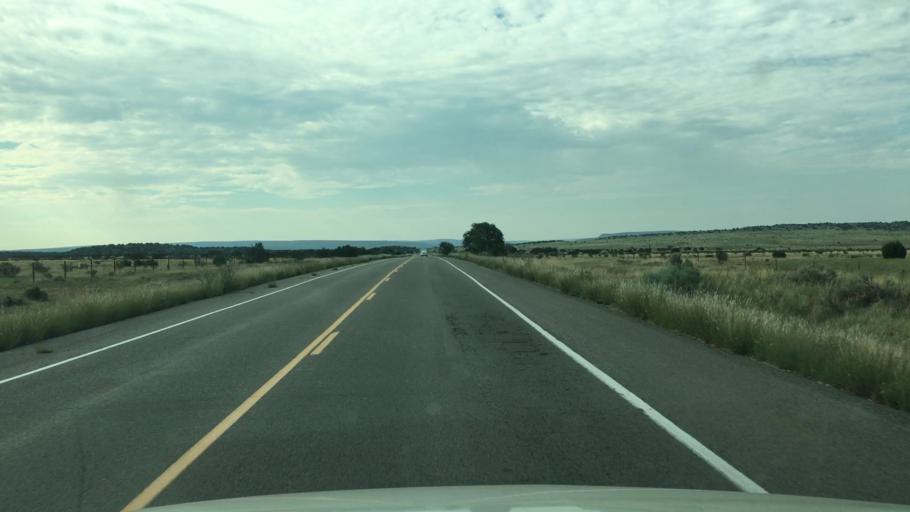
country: US
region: New Mexico
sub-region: Santa Fe County
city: Eldorado at Santa Fe
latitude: 35.4502
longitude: -105.8903
